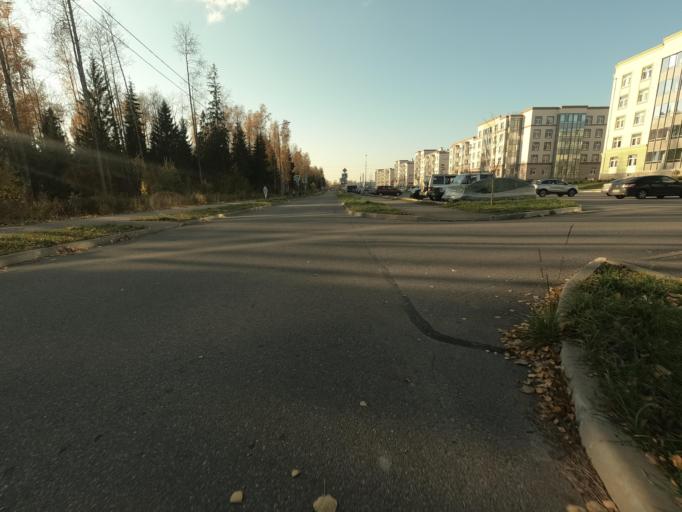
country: RU
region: Leningrad
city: Sertolovo
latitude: 60.1629
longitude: 30.1929
